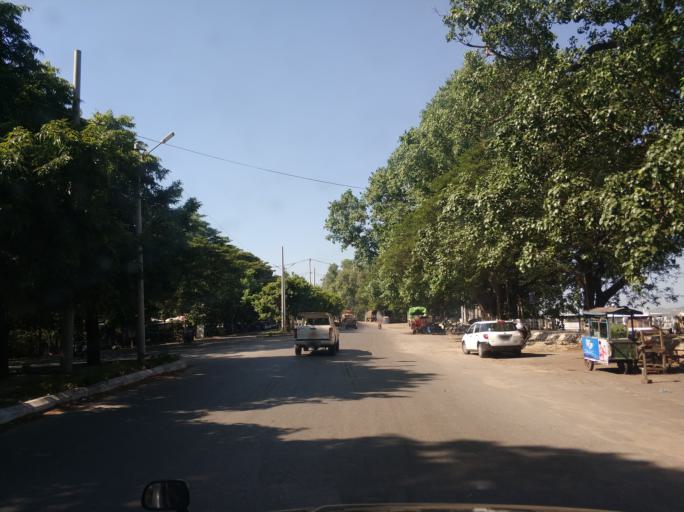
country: MM
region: Mandalay
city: Mandalay
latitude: 21.9707
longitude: 96.0564
